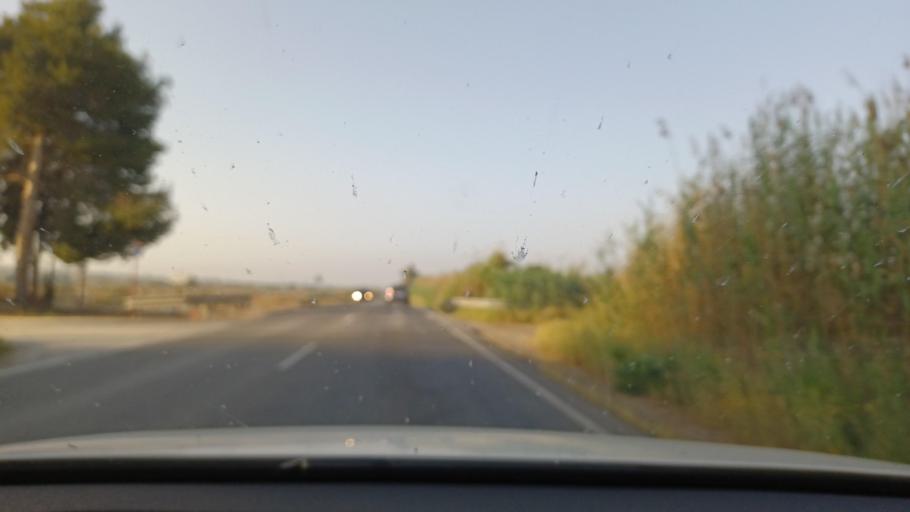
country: ES
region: Valencia
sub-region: Provincia de Alicante
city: Daya Vieja
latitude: 38.1699
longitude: -0.7024
